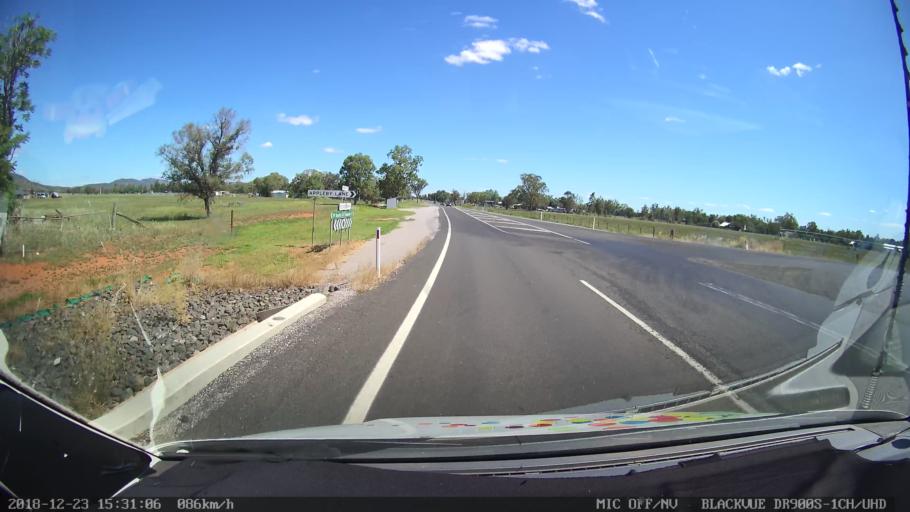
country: AU
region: New South Wales
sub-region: Tamworth Municipality
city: East Tamworth
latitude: -30.9675
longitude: 150.8664
